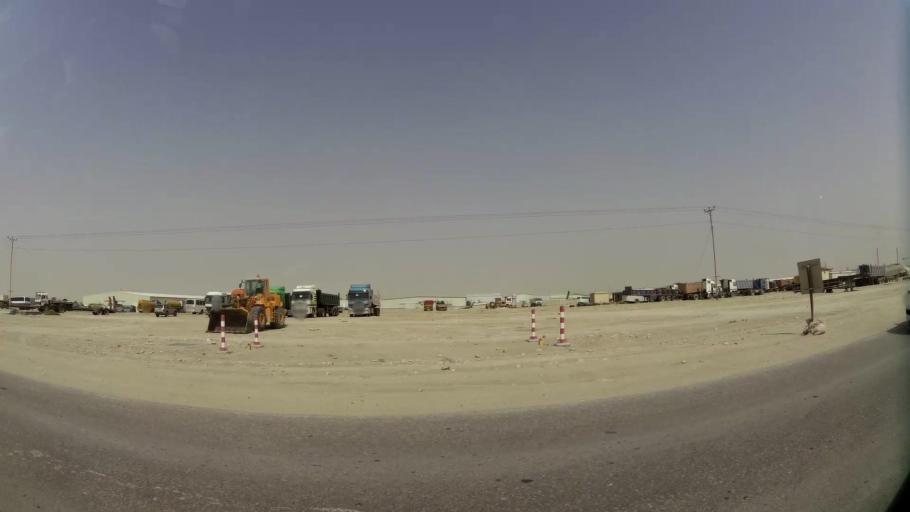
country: QA
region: Baladiyat ar Rayyan
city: Ar Rayyan
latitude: 25.2065
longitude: 51.3617
